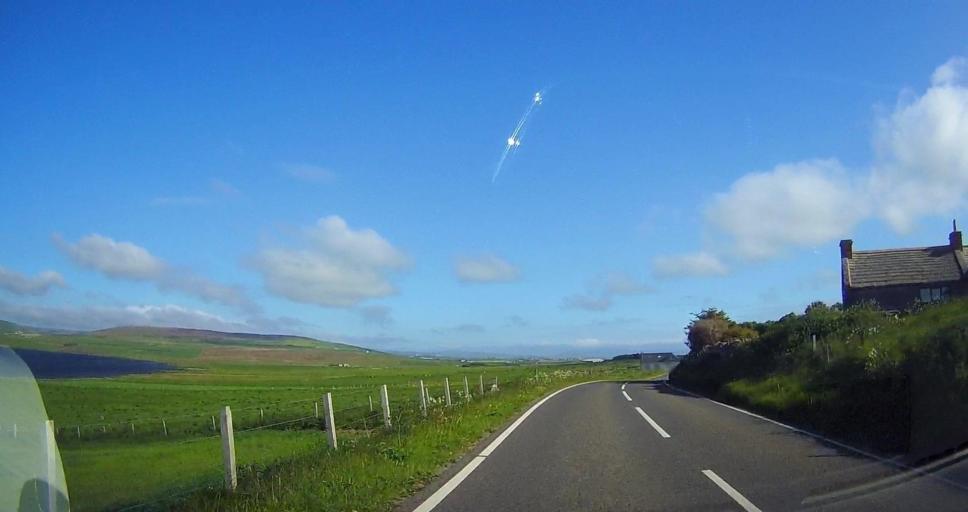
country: GB
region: Scotland
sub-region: Orkney Islands
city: Stromness
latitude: 59.1083
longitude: -3.2831
